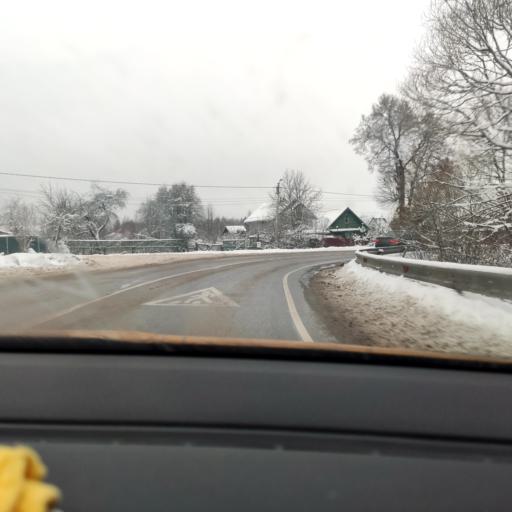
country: RU
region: Moskovskaya
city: Yershovo
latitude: 55.7522
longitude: 36.8717
